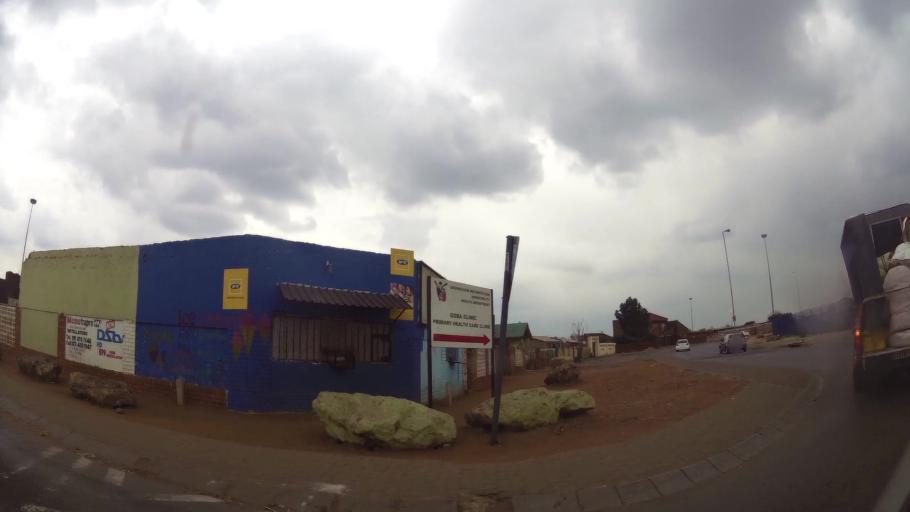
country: ZA
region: Gauteng
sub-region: Ekurhuleni Metropolitan Municipality
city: Germiston
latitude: -26.3454
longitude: 28.1498
